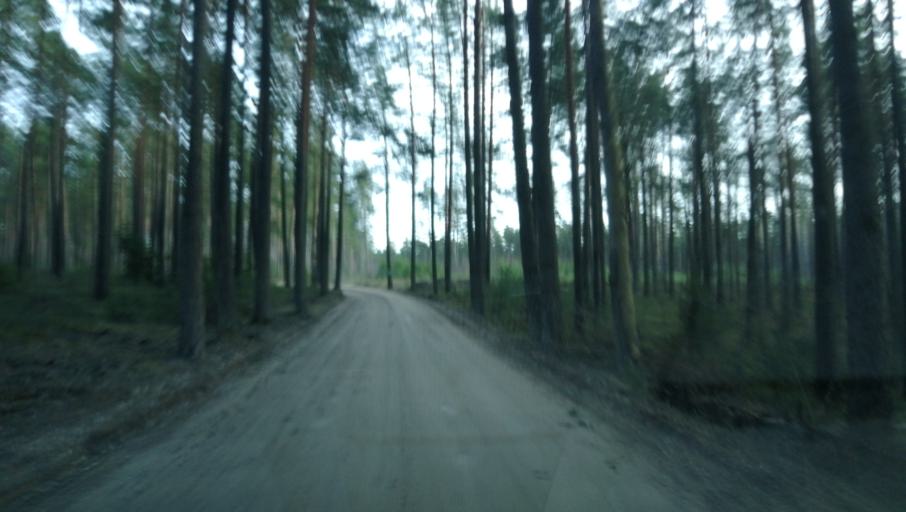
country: LV
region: Adazi
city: Adazi
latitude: 57.0542
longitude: 24.3017
